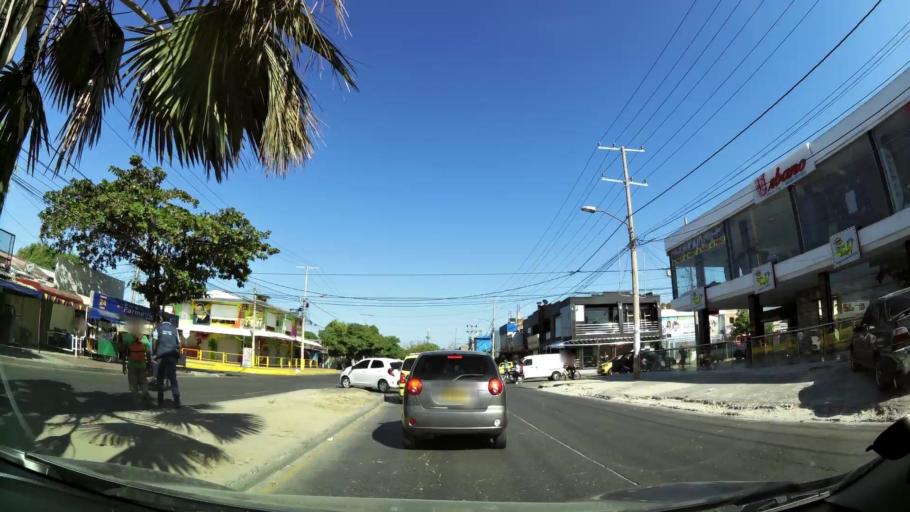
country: CO
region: Atlantico
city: Barranquilla
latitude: 10.9461
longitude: -74.7991
